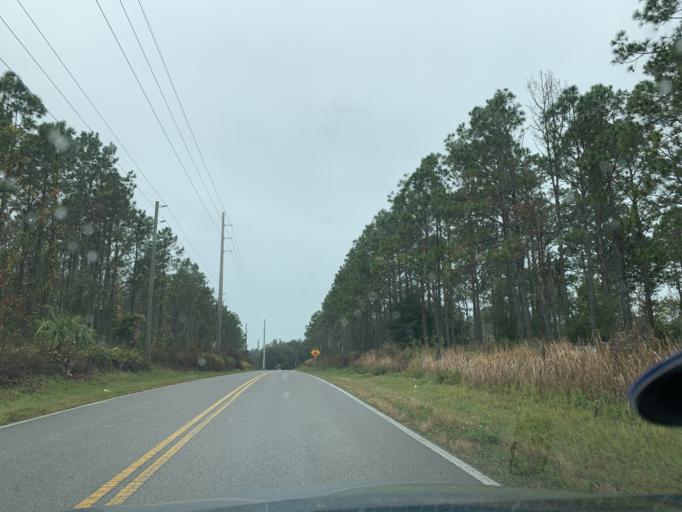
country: US
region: Florida
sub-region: Pasco County
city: Wesley Chapel
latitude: 28.2735
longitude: -82.3311
